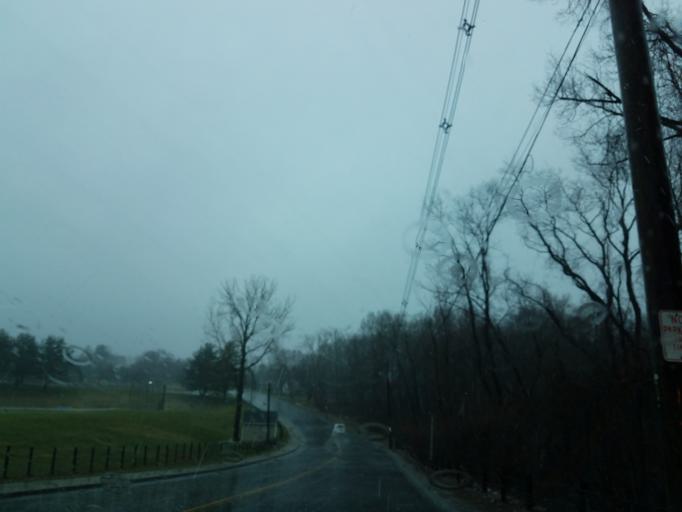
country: US
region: Connecticut
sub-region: New Haven County
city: Waterbury
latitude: 41.5337
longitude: -73.0670
